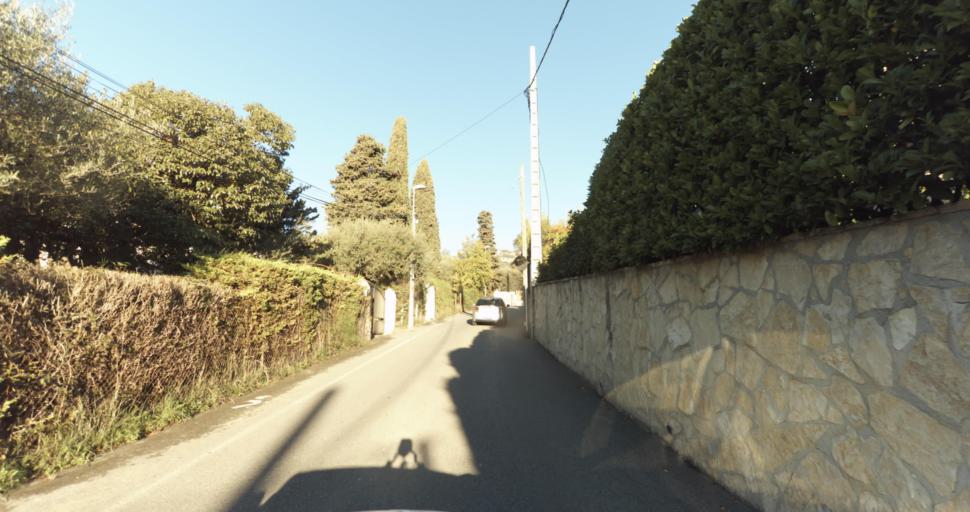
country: FR
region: Provence-Alpes-Cote d'Azur
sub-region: Departement des Alpes-Maritimes
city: Vence
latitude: 43.7186
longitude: 7.1259
